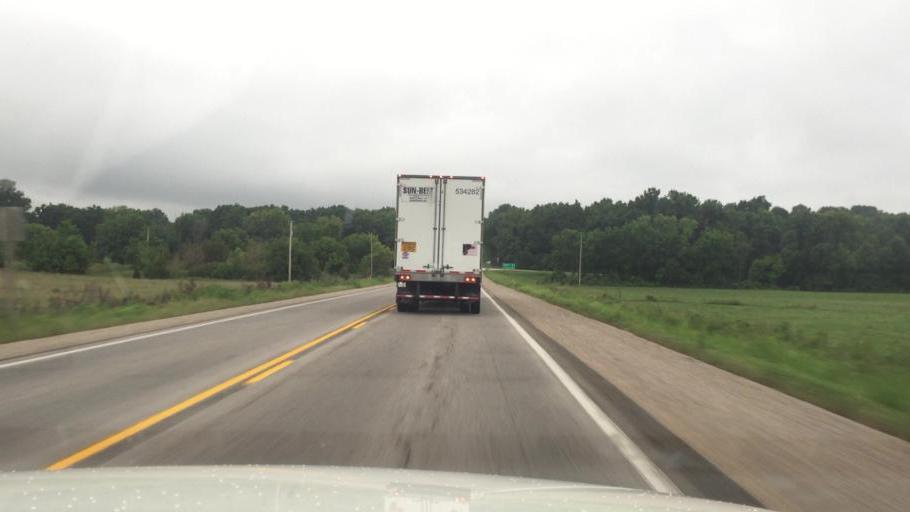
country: US
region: Kansas
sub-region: Montgomery County
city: Cherryvale
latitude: 37.1567
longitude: -95.5768
